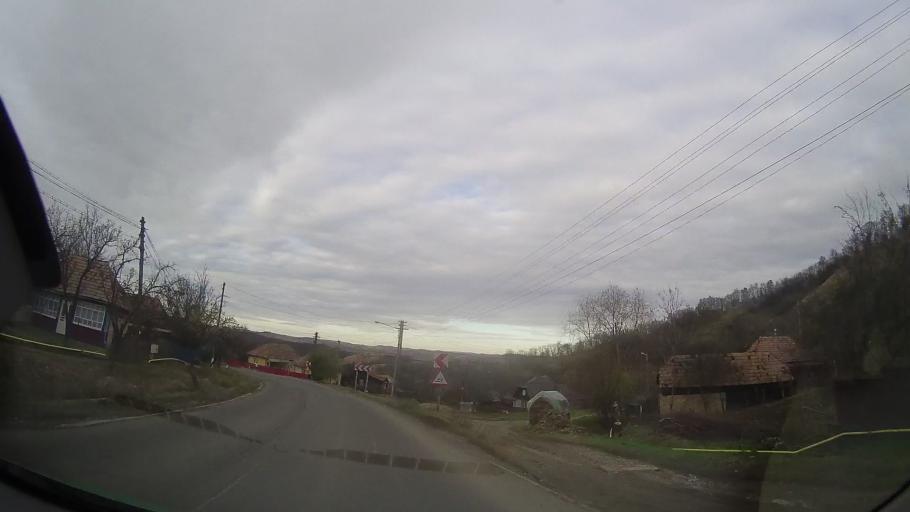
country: RO
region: Bistrita-Nasaud
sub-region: Comuna Silvasu de Campie
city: Silvasu de Campie
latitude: 46.7778
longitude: 24.3112
